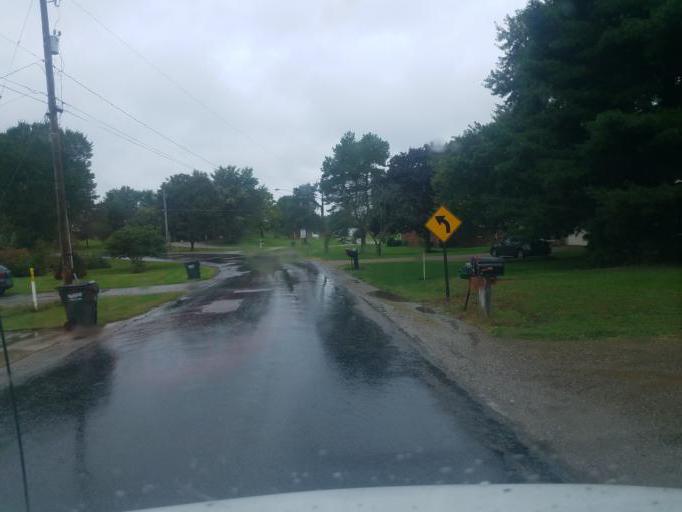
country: US
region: Ohio
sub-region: Wayne County
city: Creston
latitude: 40.9831
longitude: -81.9074
